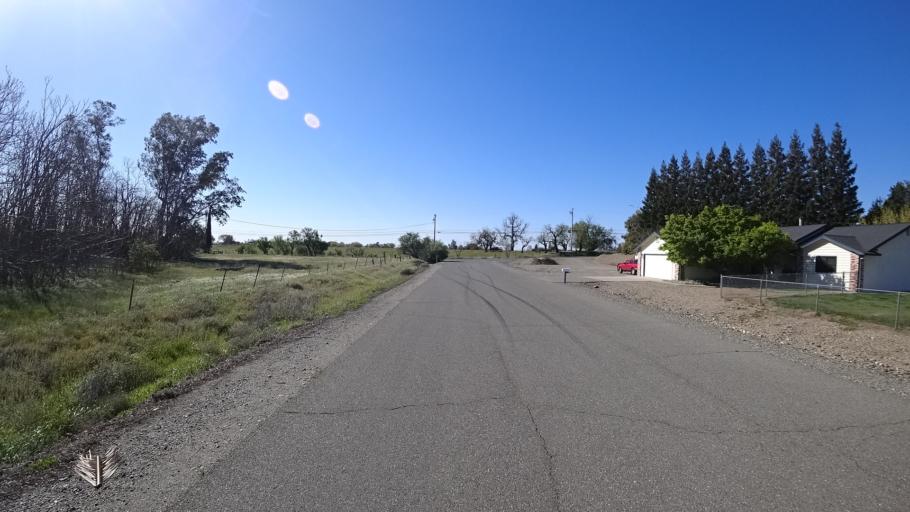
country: US
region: California
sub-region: Glenn County
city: Orland
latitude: 39.7447
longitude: -122.2133
